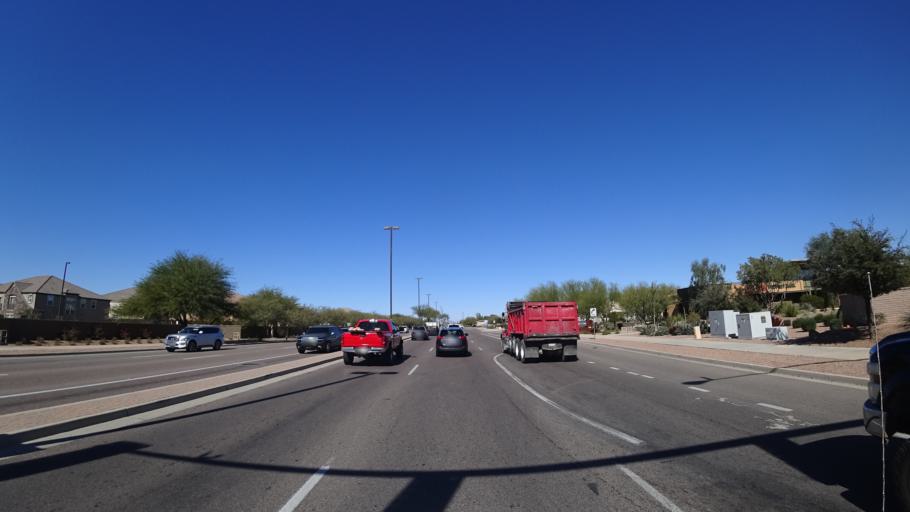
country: US
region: Arizona
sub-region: Maricopa County
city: Queen Creek
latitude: 33.2831
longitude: -111.6862
